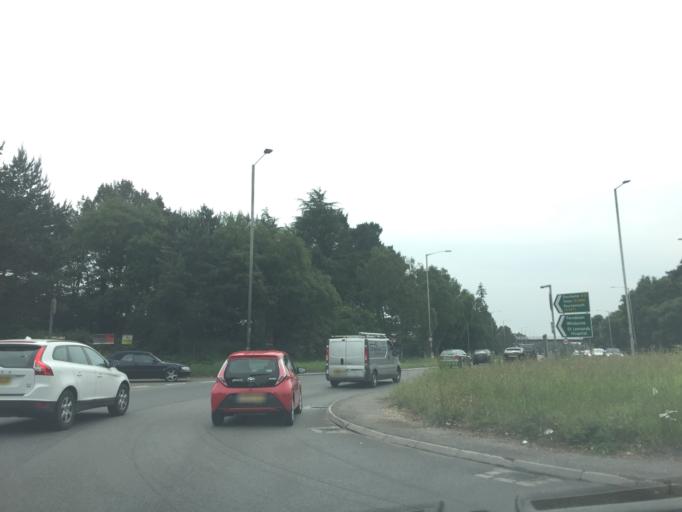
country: GB
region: England
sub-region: Dorset
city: St Leonards
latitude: 50.8209
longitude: -1.8539
